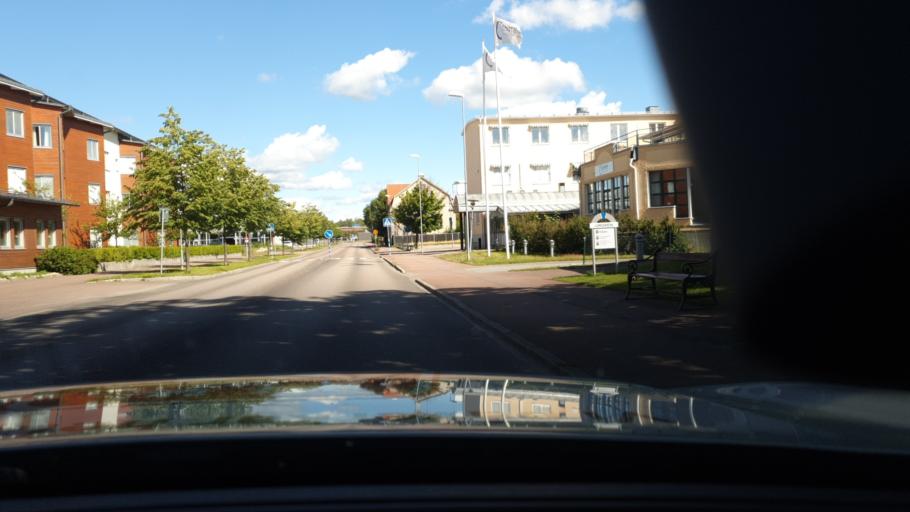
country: SE
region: Vaermland
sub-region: Kristinehamns Kommun
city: Kristinehamn
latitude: 59.3124
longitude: 14.1051
